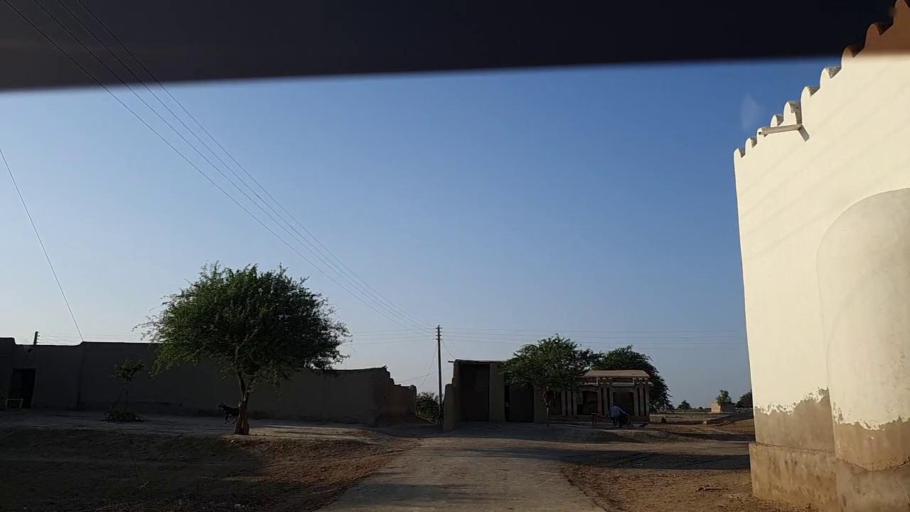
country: PK
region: Sindh
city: Johi
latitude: 26.7451
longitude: 67.6103
